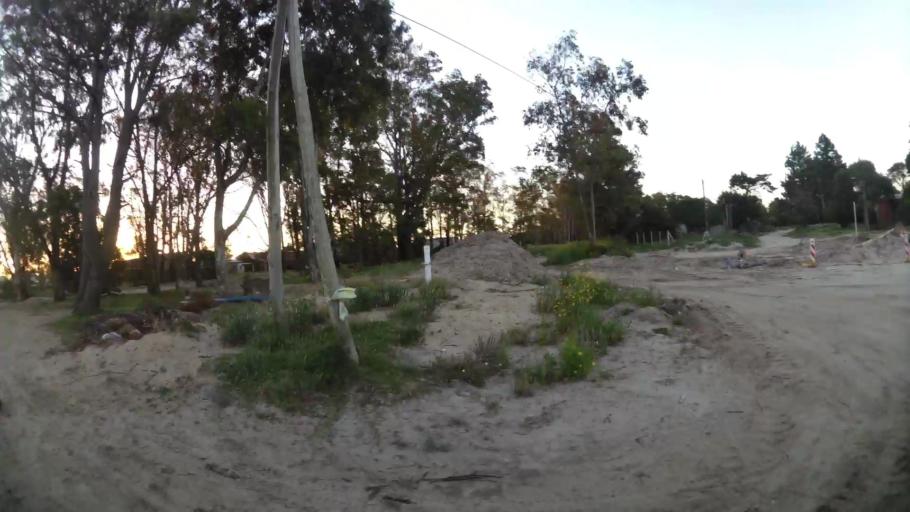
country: UY
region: Canelones
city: Barra de Carrasco
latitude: -34.8310
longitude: -55.9585
